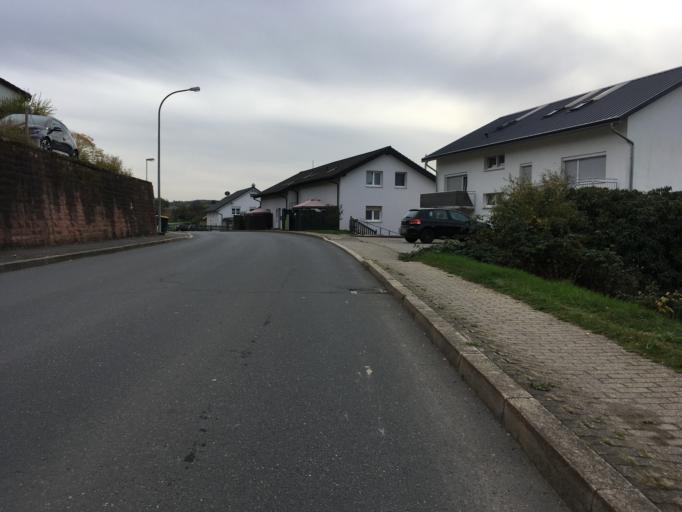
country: DE
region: Baden-Wuerttemberg
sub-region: Karlsruhe Region
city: Buchen
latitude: 49.5175
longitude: 9.3294
